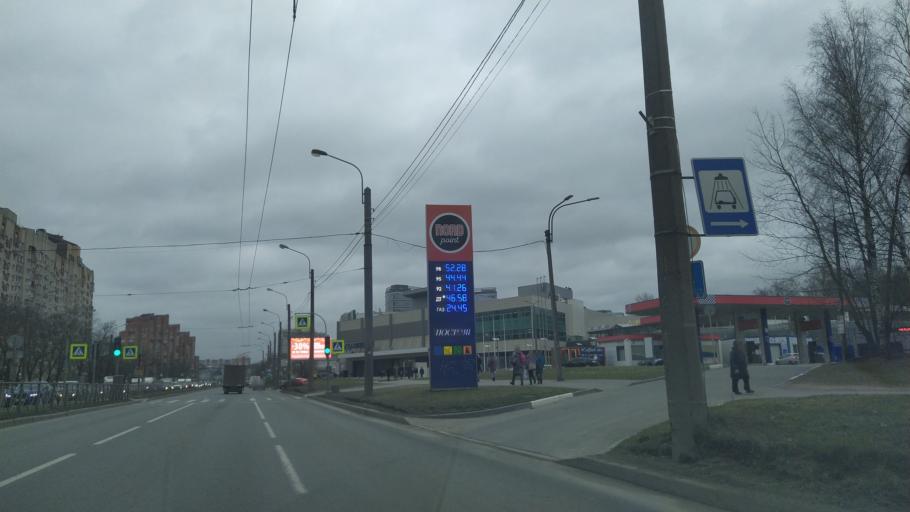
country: RU
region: St.-Petersburg
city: Kolomyagi
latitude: 60.0065
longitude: 30.2969
